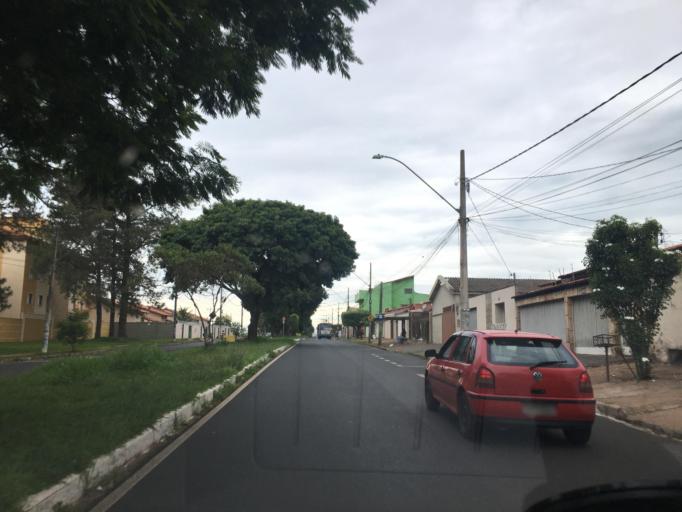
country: BR
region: Minas Gerais
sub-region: Uberlandia
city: Uberlandia
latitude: -18.9284
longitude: -48.3143
